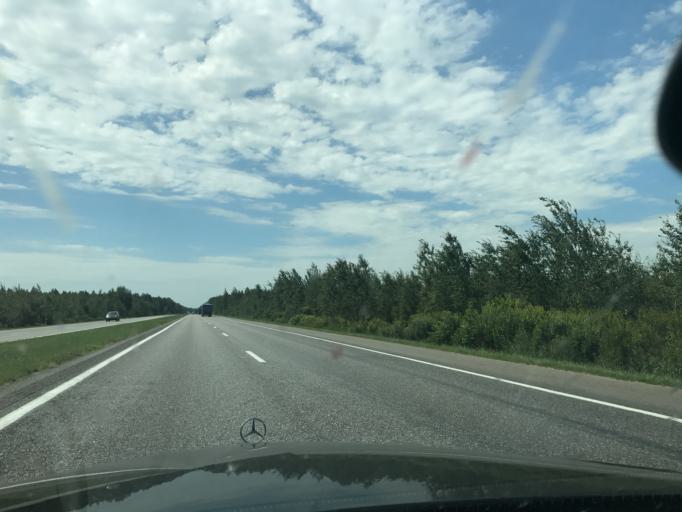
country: BY
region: Minsk
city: Horad Barysaw
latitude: 54.1044
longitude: 28.5030
